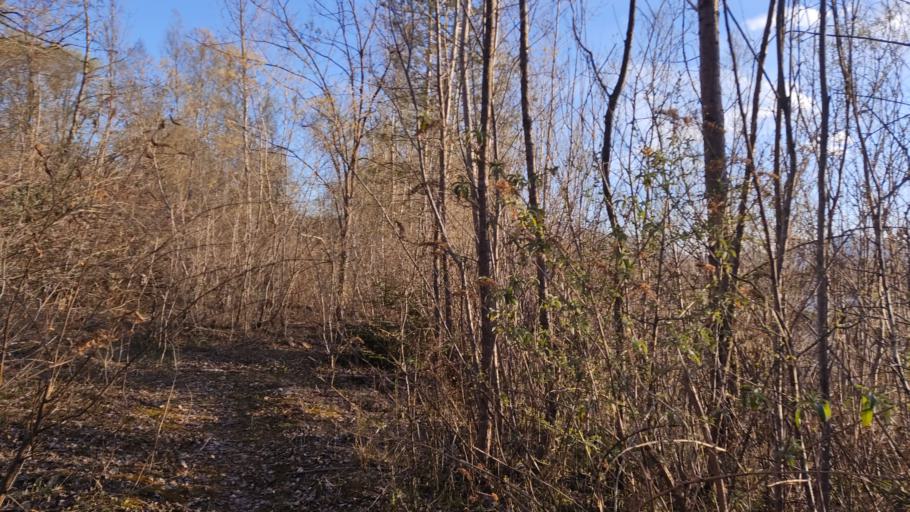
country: IT
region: Veneto
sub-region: Provincia di Belluno
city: Sedico
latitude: 46.0992
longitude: 12.0813
